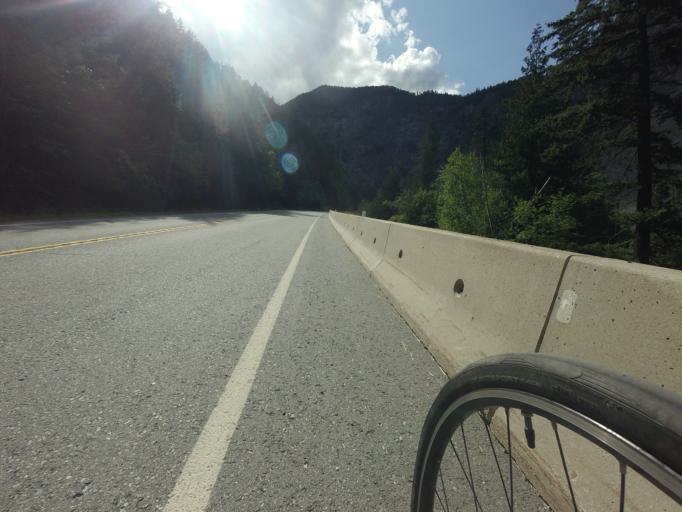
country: CA
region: British Columbia
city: Lillooet
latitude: 50.6453
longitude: -122.0609
